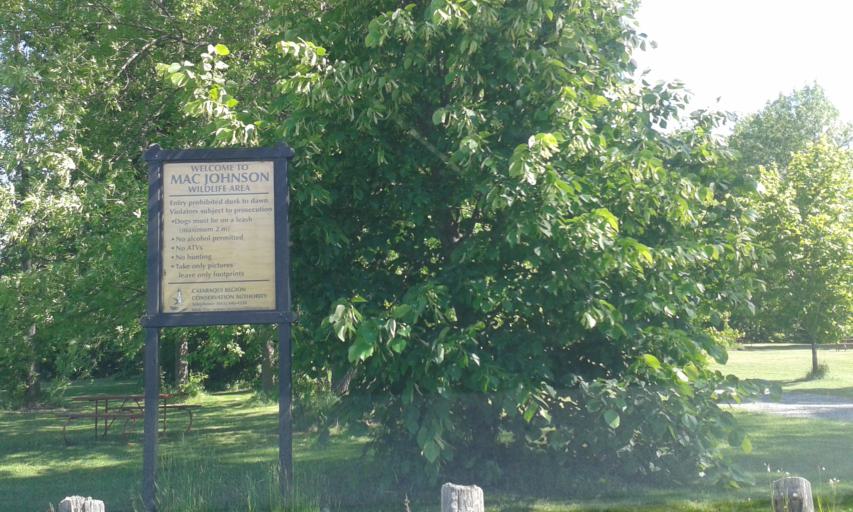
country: CA
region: Ontario
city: Brockville
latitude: 44.6303
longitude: -75.7302
